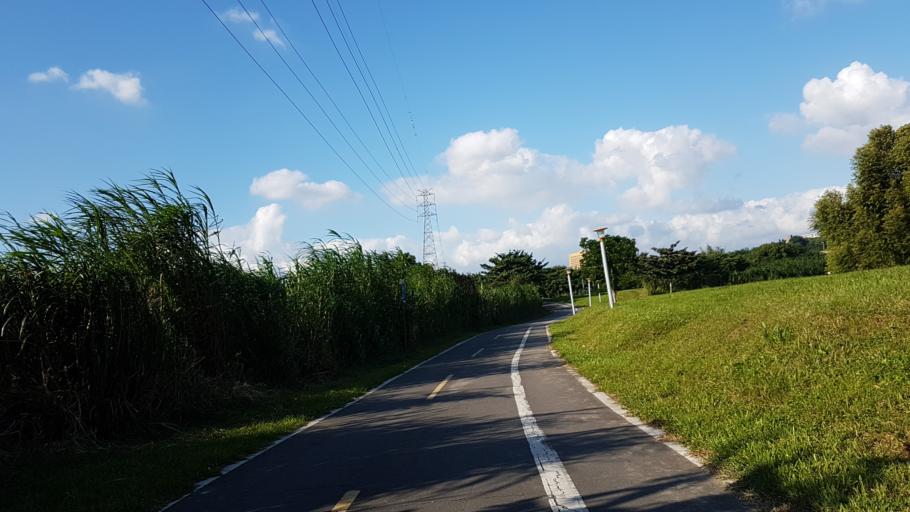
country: TW
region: Taipei
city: Taipei
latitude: 25.0033
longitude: 121.5307
